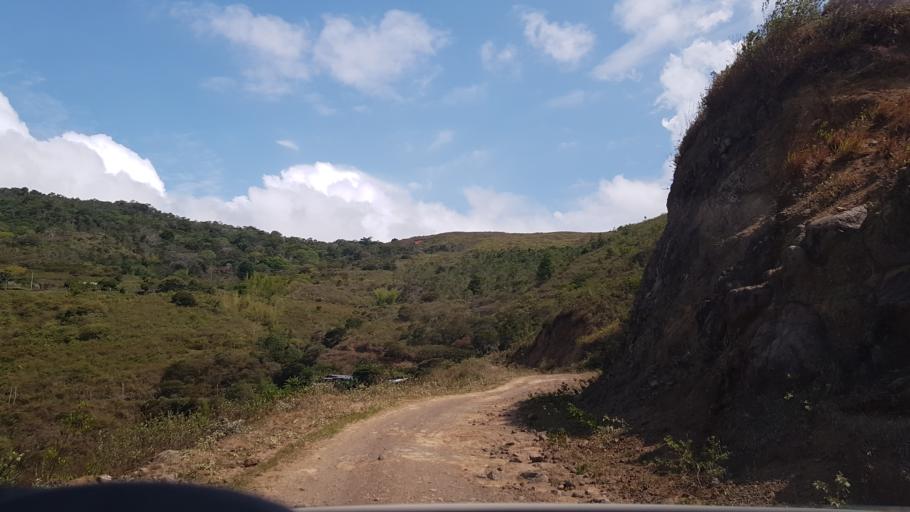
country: CO
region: Valle del Cauca
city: Yumbo
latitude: 3.6513
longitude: -76.5118
